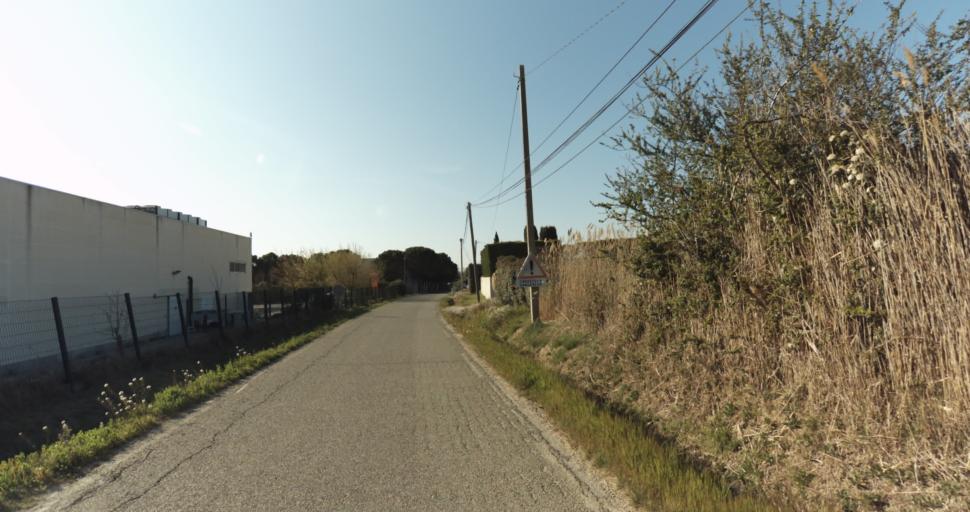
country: FR
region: Provence-Alpes-Cote d'Azur
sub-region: Departement des Bouches-du-Rhone
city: Bouc-Bel-Air
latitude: 43.4880
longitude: 5.3882
